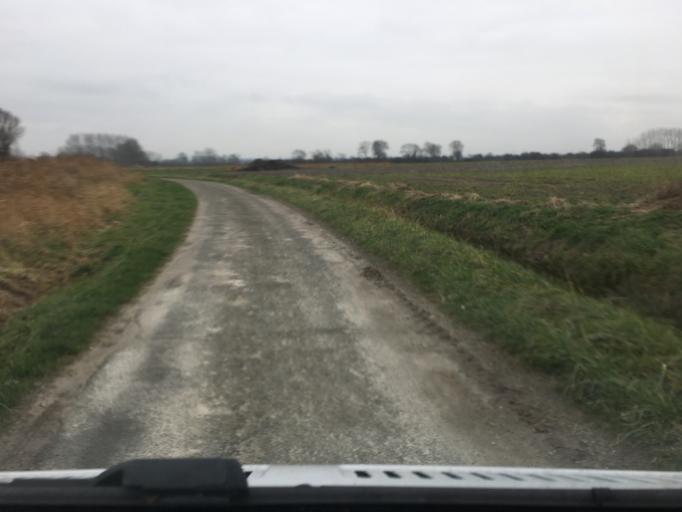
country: FR
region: Picardie
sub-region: Departement de la Somme
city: Pende
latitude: 50.1766
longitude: 1.5430
